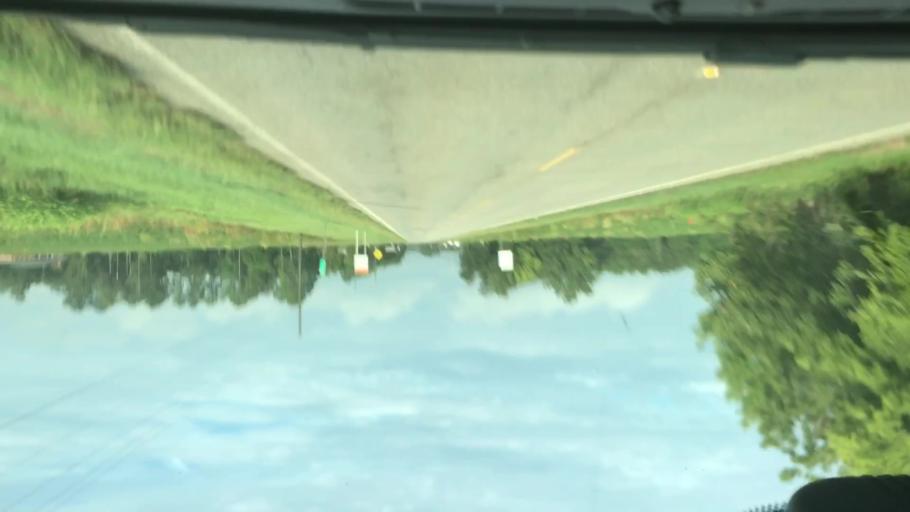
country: US
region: Georgia
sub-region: Quitman County
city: Georgetown
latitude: 31.7593
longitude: -85.0707
